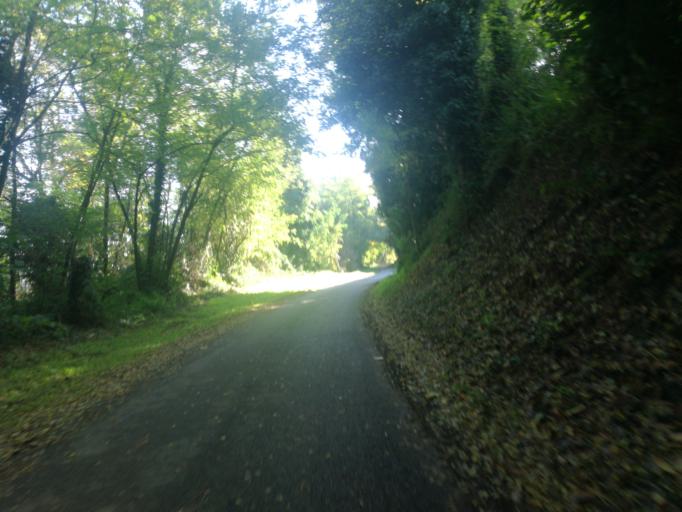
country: IT
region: Lombardy
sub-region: Provincia di Bergamo
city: Bottanuco
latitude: 45.6252
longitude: 9.5045
